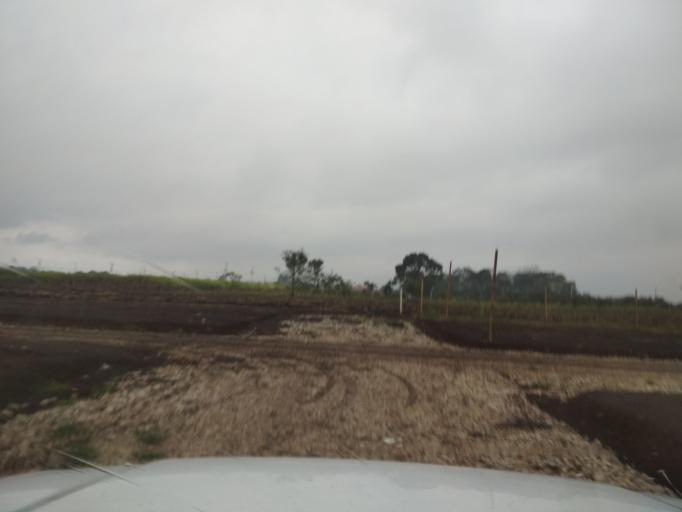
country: MX
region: Veracruz
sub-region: Cordoba
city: Veinte de Noviembre
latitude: 18.8587
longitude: -96.9622
